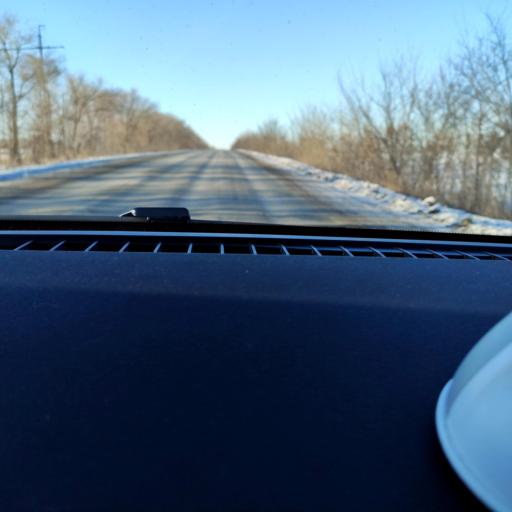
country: RU
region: Samara
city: Spiridonovka
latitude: 53.1446
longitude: 50.5344
